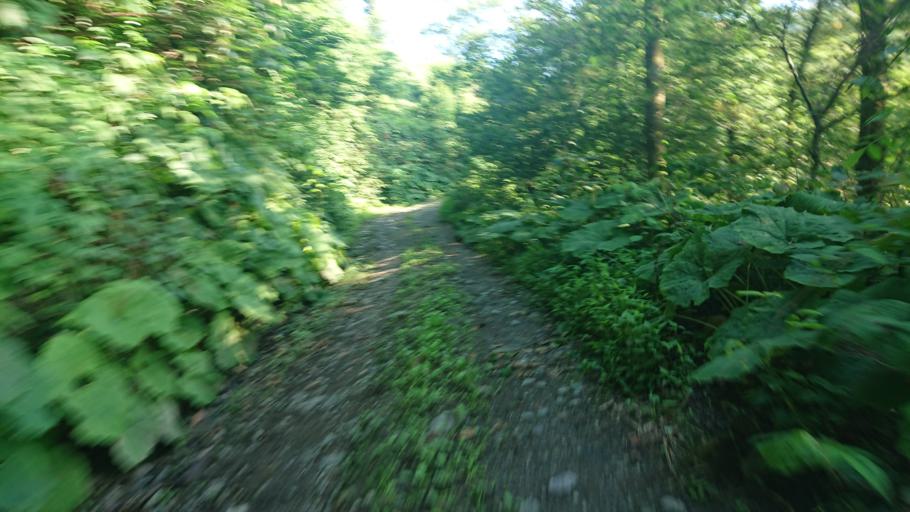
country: TR
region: Rize
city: Rize
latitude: 40.9761
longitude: 40.4988
